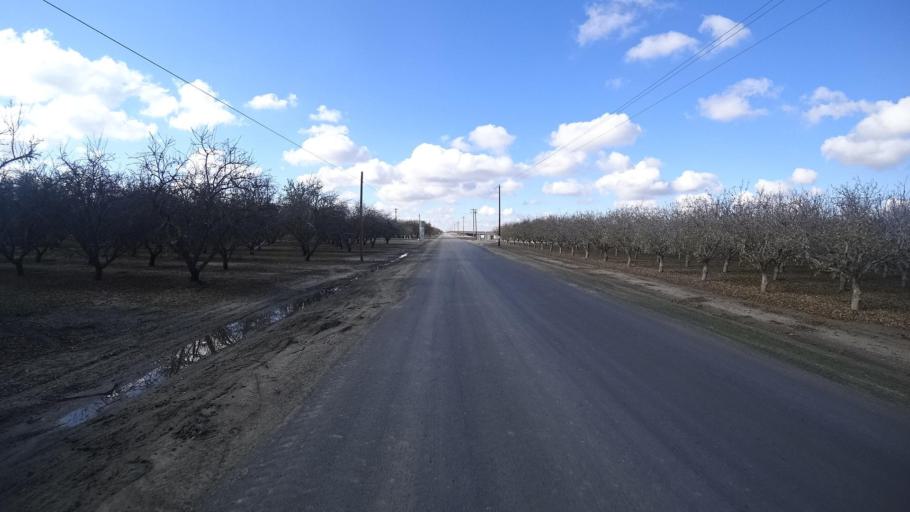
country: US
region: California
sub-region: Kern County
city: McFarland
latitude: 35.6886
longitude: -119.3018
